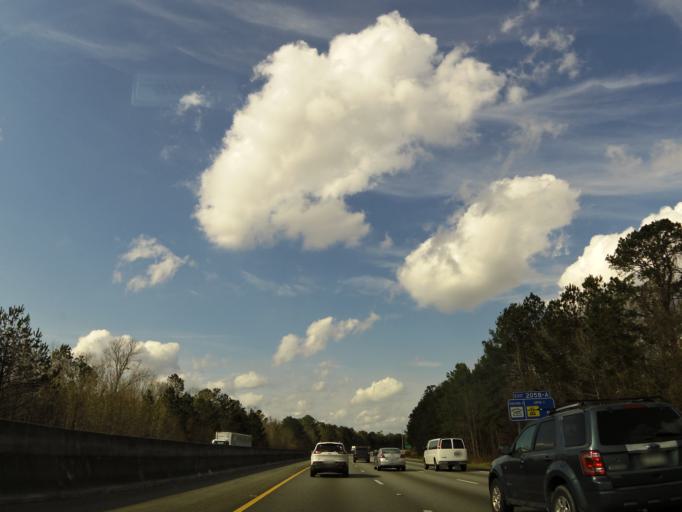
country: US
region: South Carolina
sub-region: Berkeley County
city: Goose Creek
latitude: 32.9600
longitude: -80.0706
